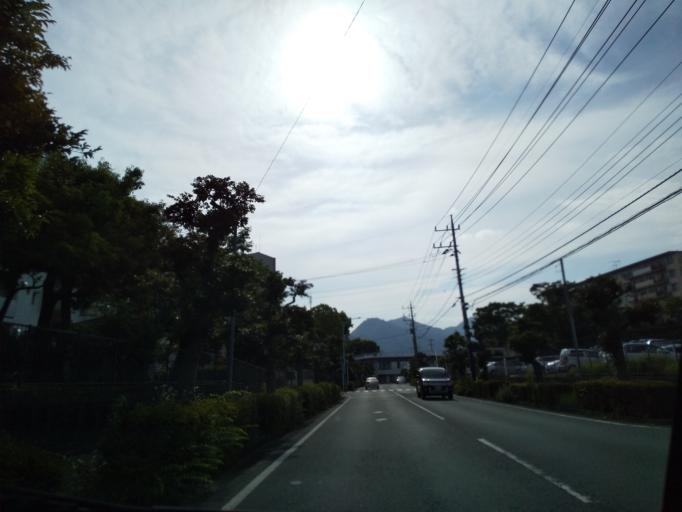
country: JP
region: Kanagawa
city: Zama
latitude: 35.4912
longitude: 139.3289
